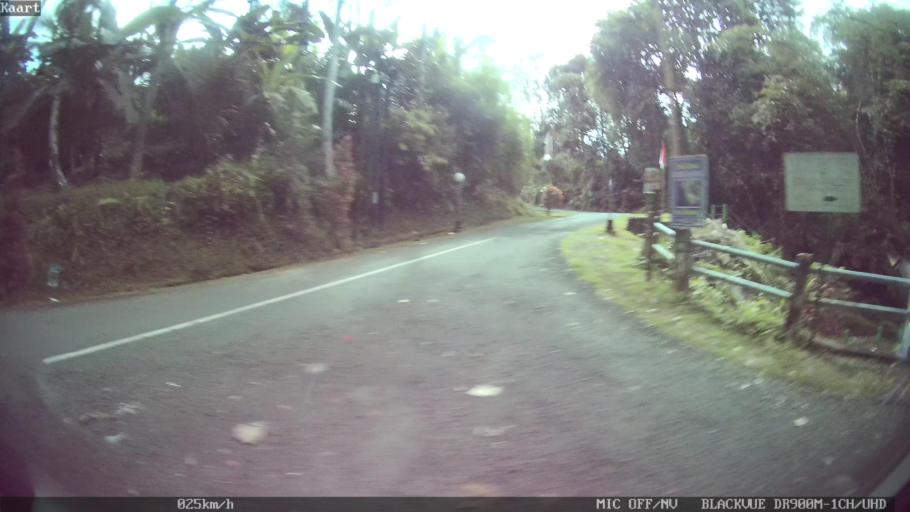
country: ID
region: Bali
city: Banjar Pesalakan
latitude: -8.5059
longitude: 115.3024
